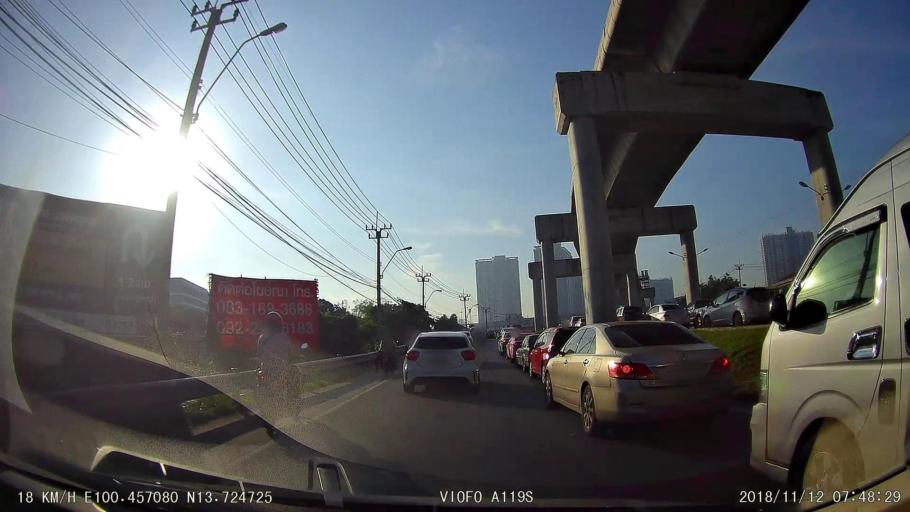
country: TH
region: Bangkok
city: Bangkok Yai
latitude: 13.7241
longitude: 100.4574
